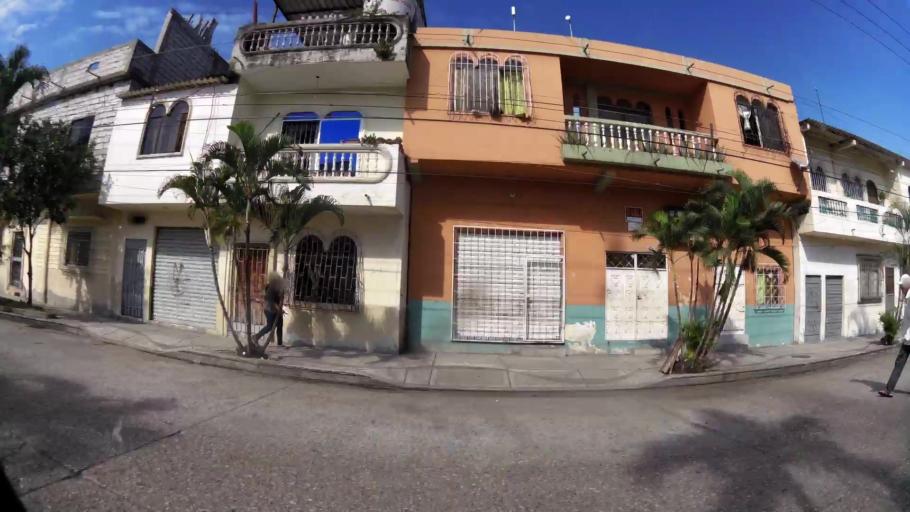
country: EC
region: Guayas
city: Guayaquil
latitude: -2.2115
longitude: -79.9123
